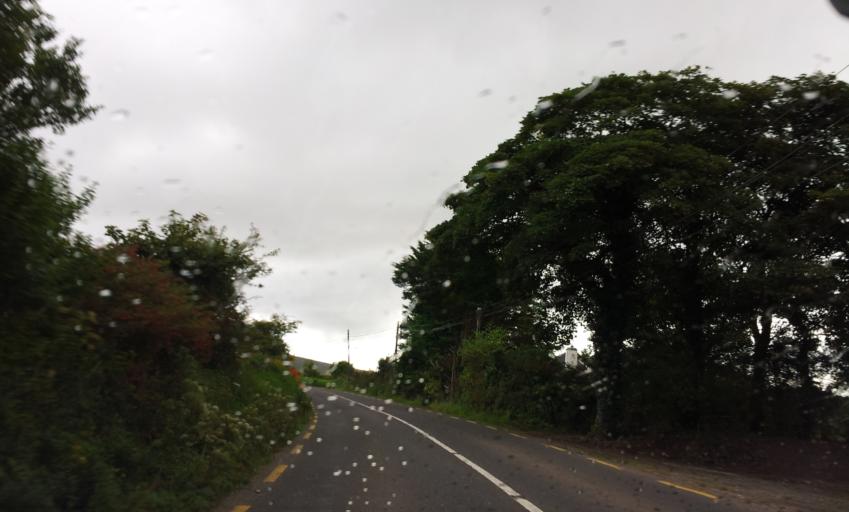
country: IE
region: Munster
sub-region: Ciarrai
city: Killorglin
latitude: 52.1799
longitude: -9.9751
